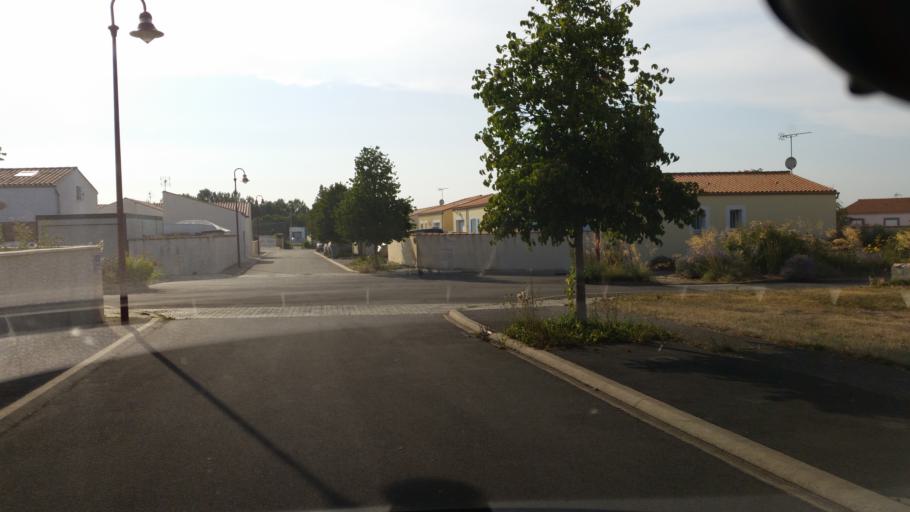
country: FR
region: Poitou-Charentes
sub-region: Departement de la Charente-Maritime
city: Marans
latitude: 46.3090
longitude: -1.0038
